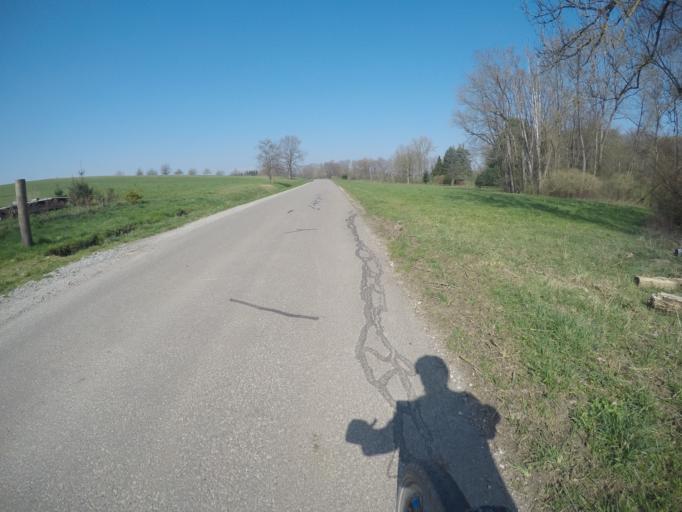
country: DE
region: Baden-Wuerttemberg
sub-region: Tuebingen Region
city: Pliezhausen
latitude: 48.5743
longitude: 9.2073
